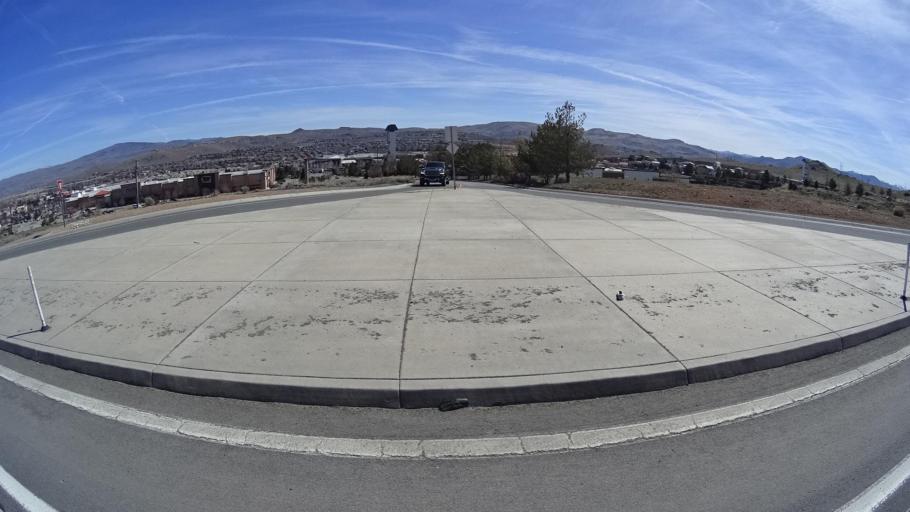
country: US
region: Nevada
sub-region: Washoe County
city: Sun Valley
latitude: 39.5791
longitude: -119.7450
